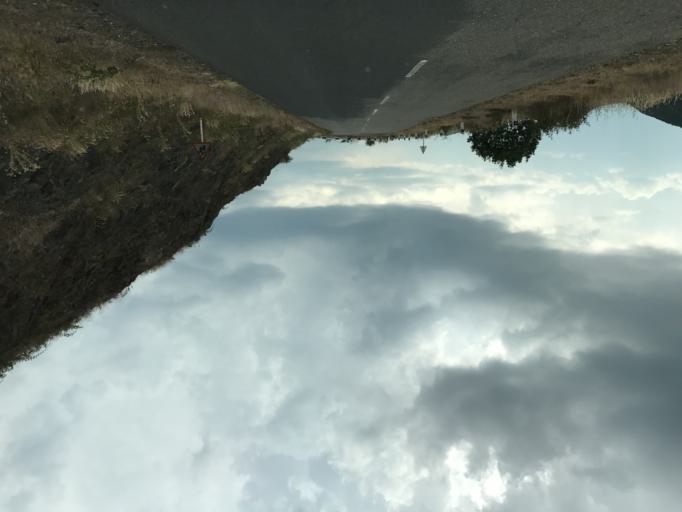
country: AZ
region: Lacin
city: Lacin
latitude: 39.6777
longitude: 46.6306
